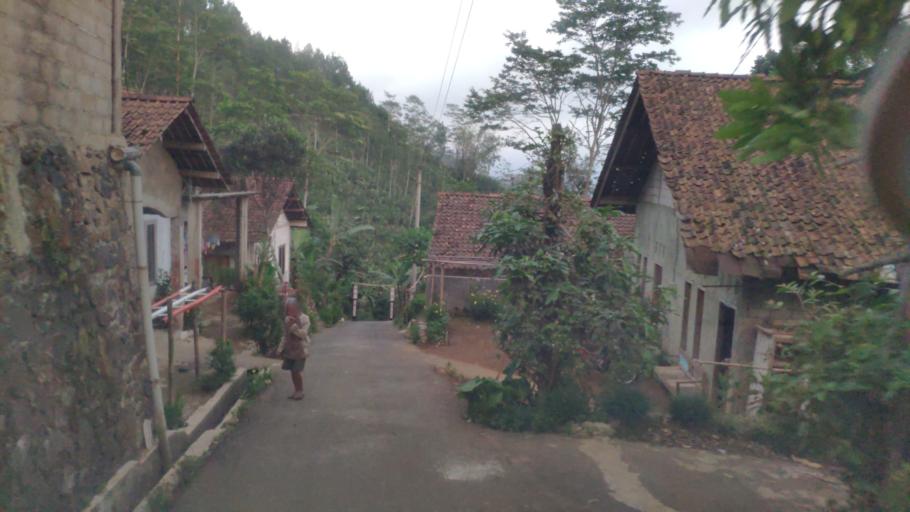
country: ID
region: Central Java
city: Wonosobo
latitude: -7.2977
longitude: 109.7178
